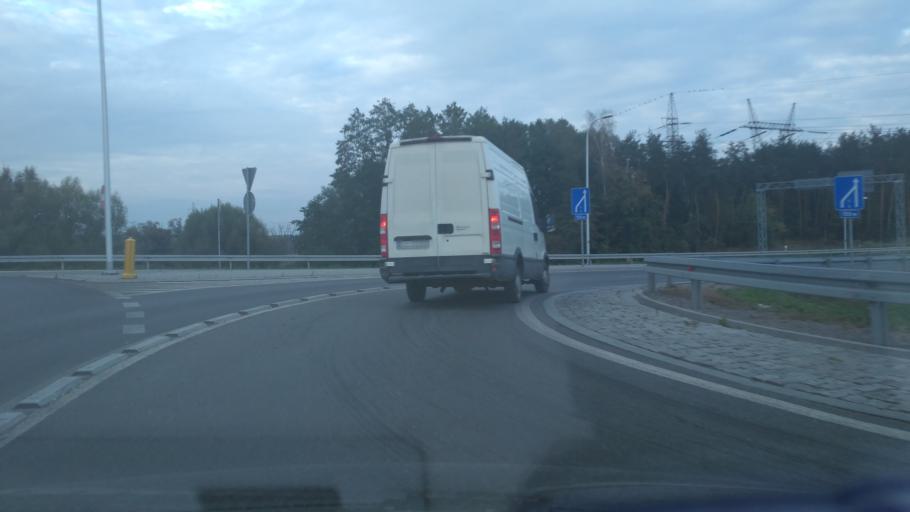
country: PL
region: Lublin Voivodeship
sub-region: Powiat lubelski
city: Jakubowice Murowane
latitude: 51.2759
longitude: 22.6534
